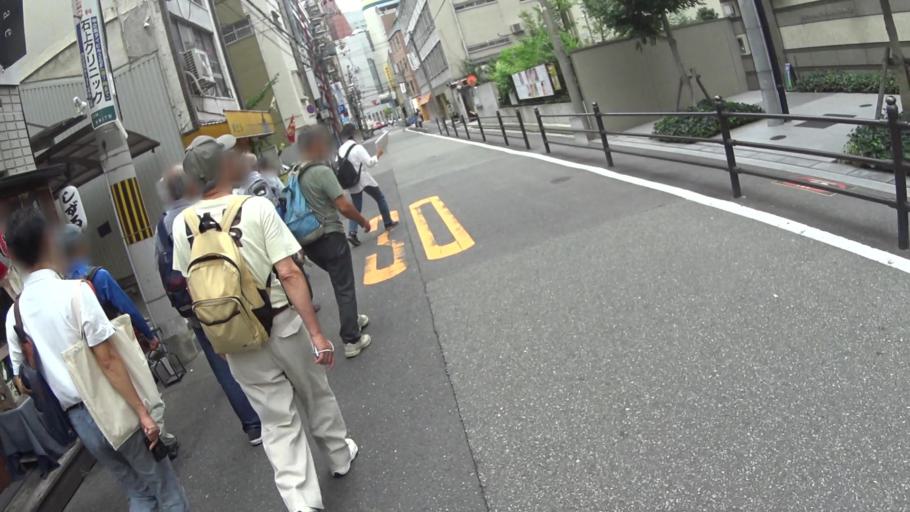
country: JP
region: Osaka
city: Osaka-shi
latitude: 34.6966
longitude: 135.4938
